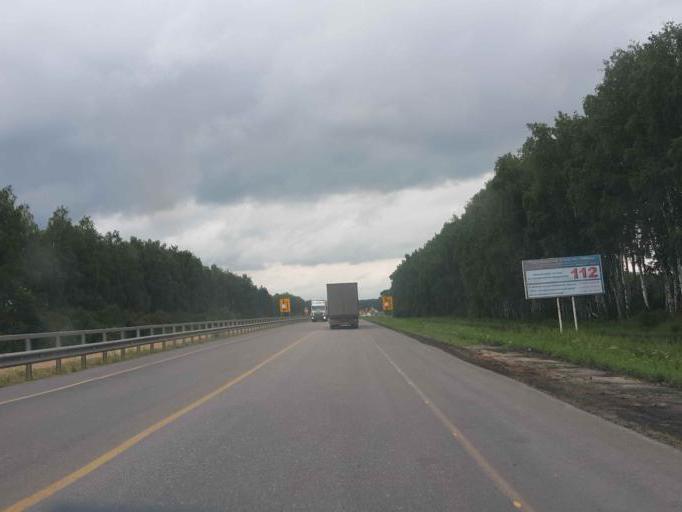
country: RU
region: Tambov
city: Selezni
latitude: 52.7951
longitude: 41.0005
